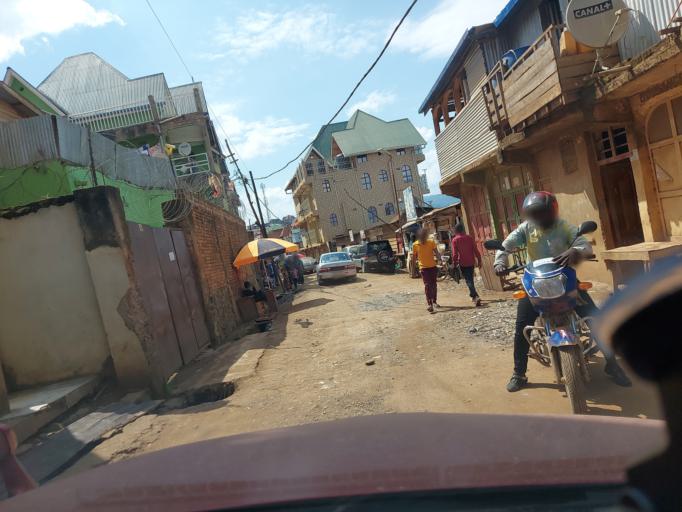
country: RW
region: Western Province
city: Cyangugu
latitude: -2.5016
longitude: 28.8770
